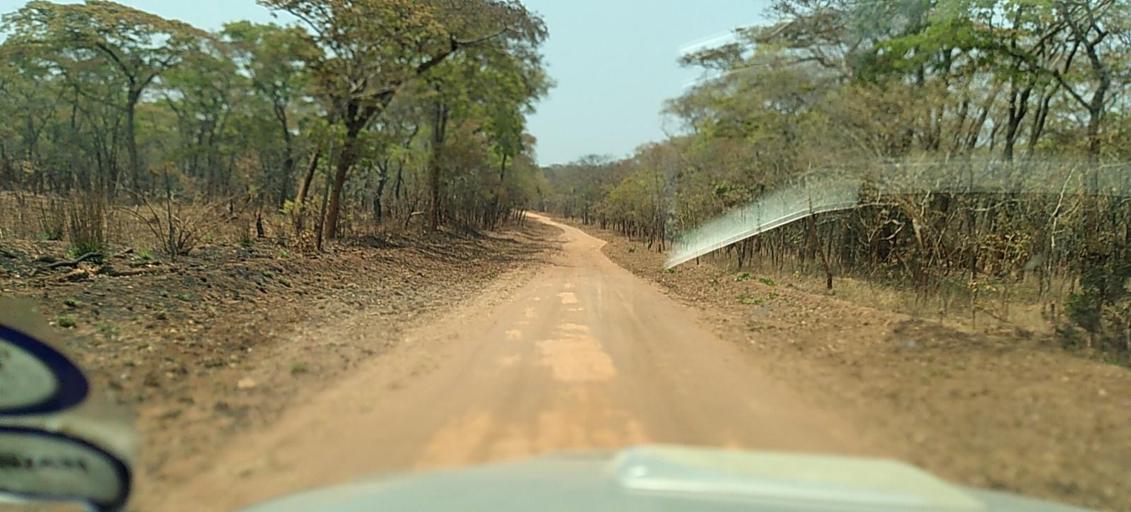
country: ZM
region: North-Western
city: Kasempa
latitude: -13.5508
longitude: 26.0634
